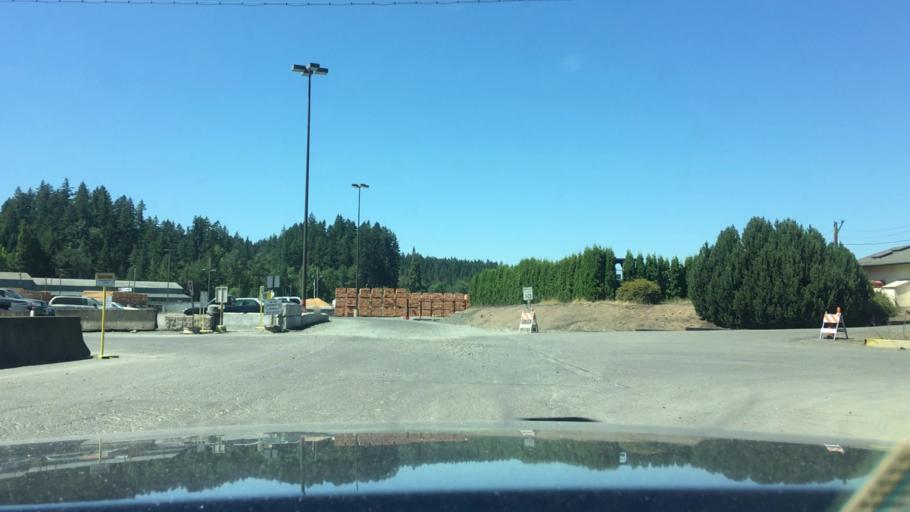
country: US
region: Oregon
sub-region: Lane County
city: Cottage Grove
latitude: 43.7669
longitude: -123.0775
